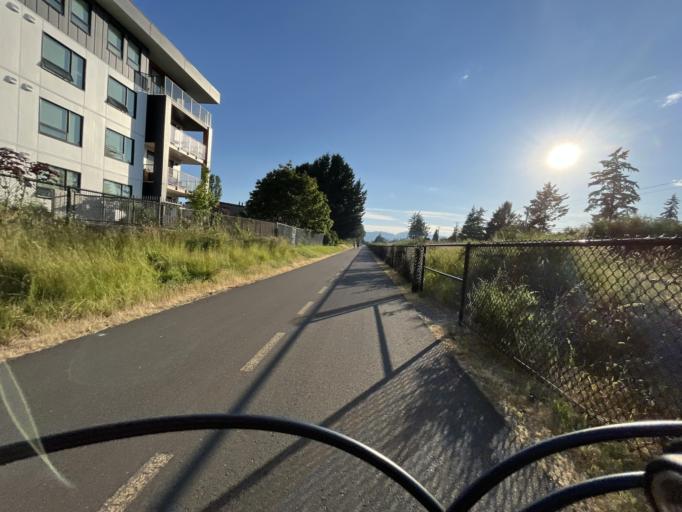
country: CA
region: British Columbia
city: Langford
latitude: 48.4484
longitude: -123.4898
